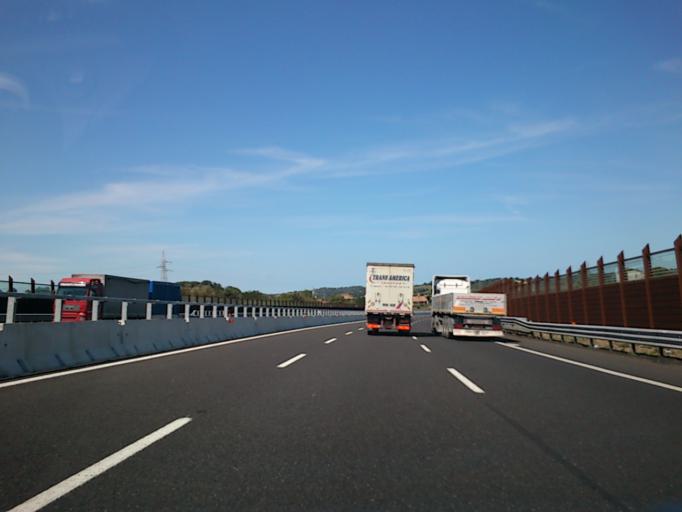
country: IT
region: The Marches
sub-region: Provincia di Pesaro e Urbino
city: Rosciano
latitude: 43.8233
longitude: 12.9998
